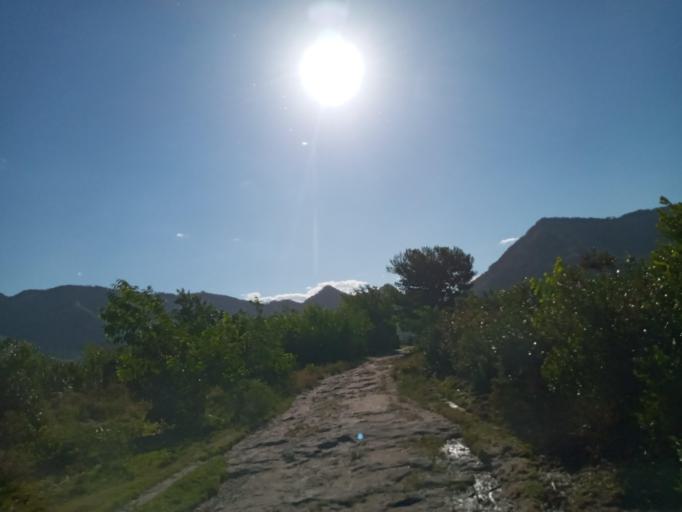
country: MG
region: Anosy
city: Fort Dauphin
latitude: -24.8292
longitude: 47.0490
